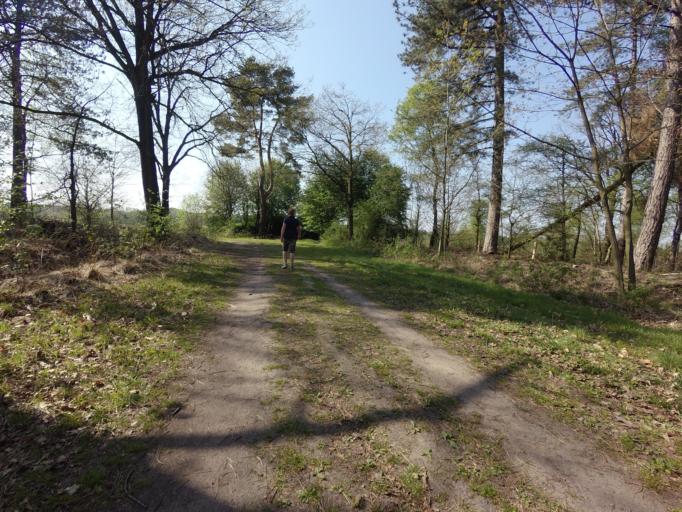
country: NL
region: North Brabant
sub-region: Gemeente Goirle
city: Goirle
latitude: 51.4951
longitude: 5.0193
